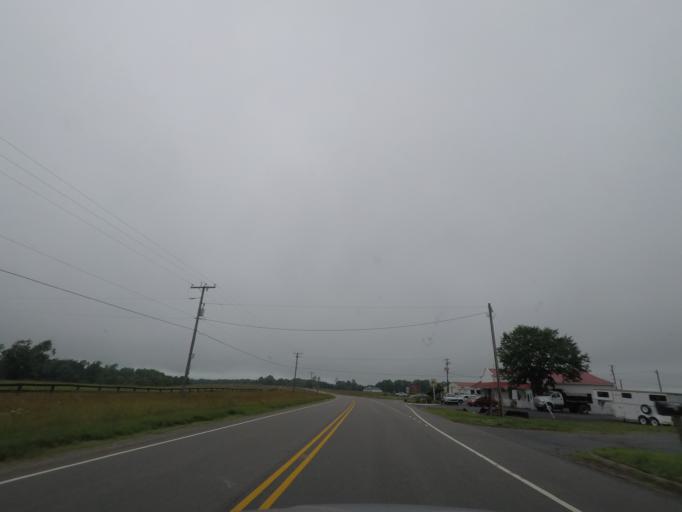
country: US
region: Virginia
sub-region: Fluvanna County
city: Weber City
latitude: 37.6131
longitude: -78.3804
